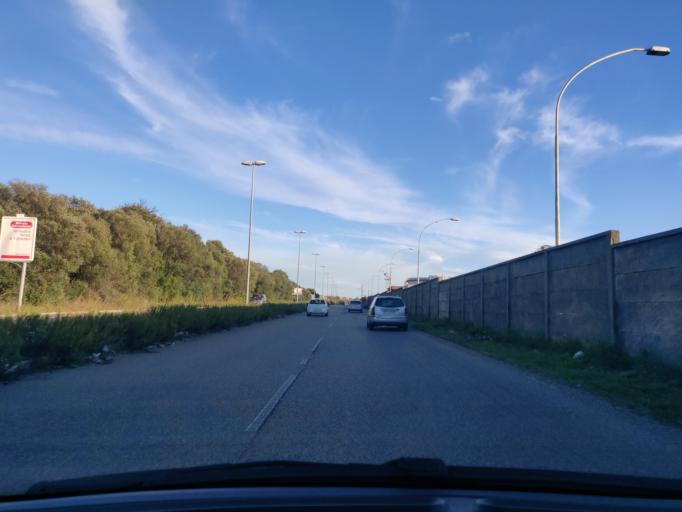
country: IT
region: Latium
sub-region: Citta metropolitana di Roma Capitale
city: Civitavecchia
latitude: 42.1130
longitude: 11.7808
